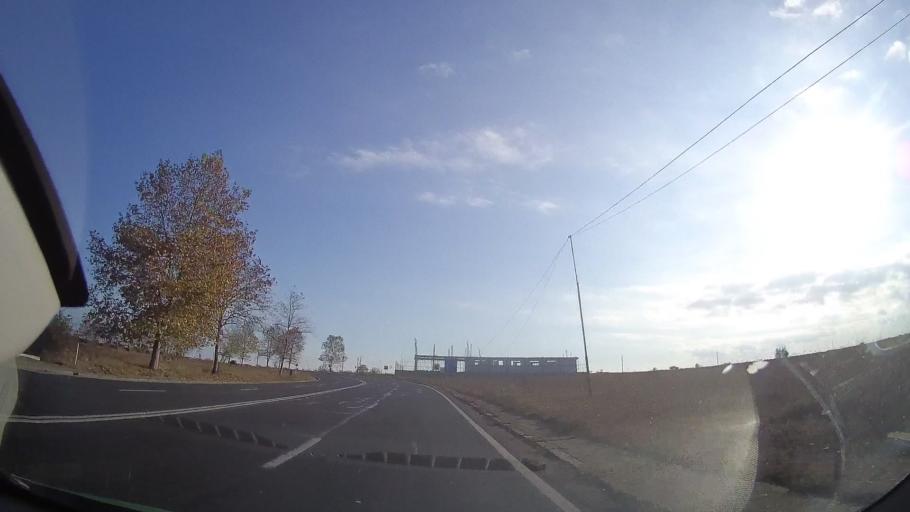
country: RO
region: Constanta
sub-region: Municipiul Mangalia
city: Mangalia
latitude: 43.7946
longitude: 28.5605
